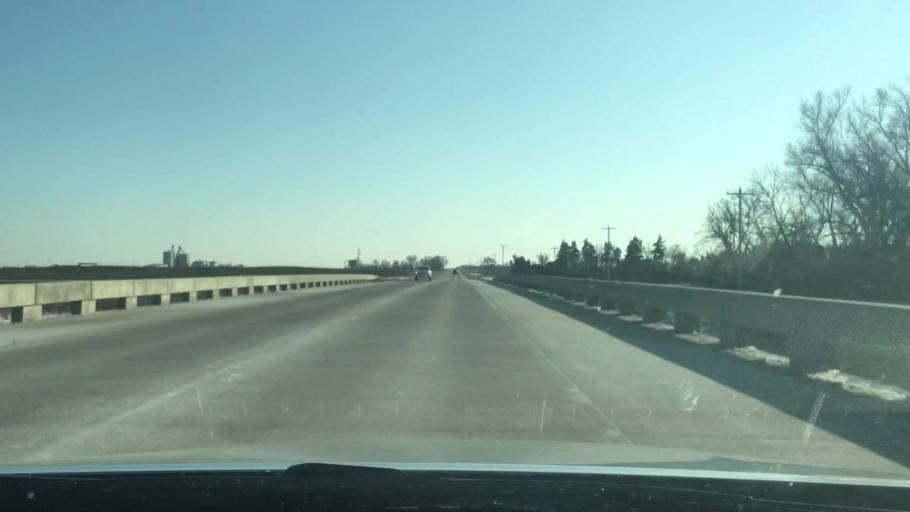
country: US
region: Kansas
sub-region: Rice County
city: Lyons
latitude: 38.3068
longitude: -98.2019
